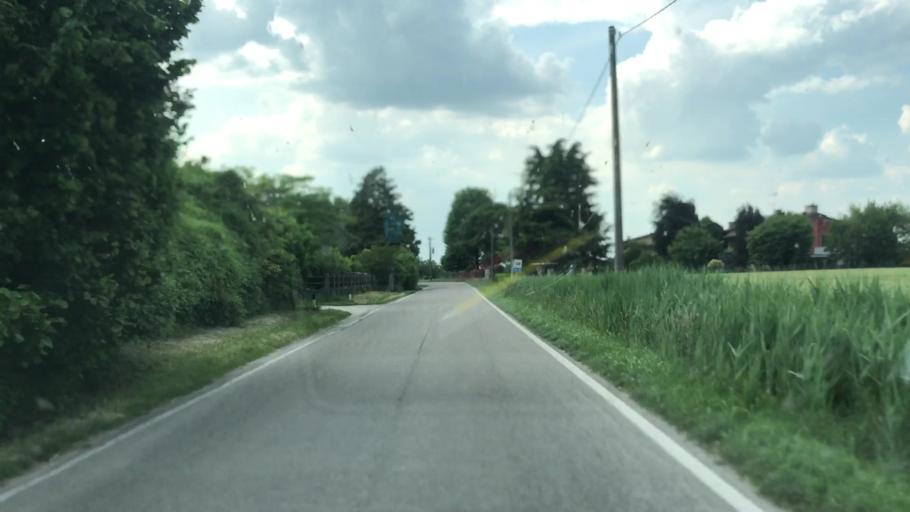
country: IT
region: Lombardy
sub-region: Provincia di Mantova
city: Castel Goffredo
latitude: 45.2925
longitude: 10.5011
